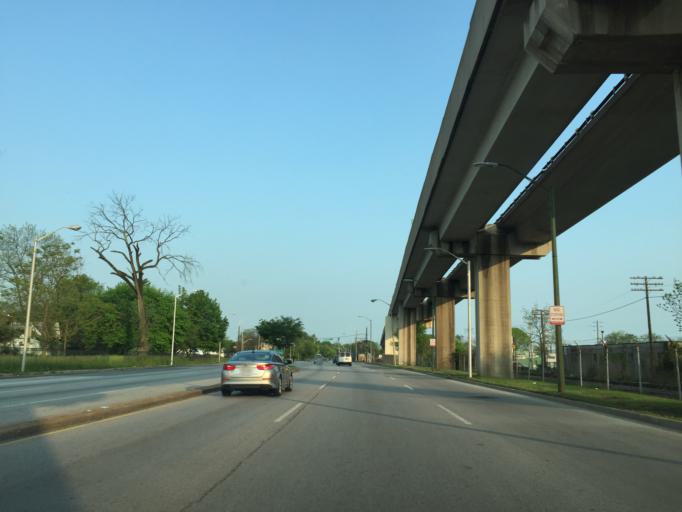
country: US
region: Maryland
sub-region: Baltimore County
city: Lochearn
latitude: 39.3414
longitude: -76.6833
